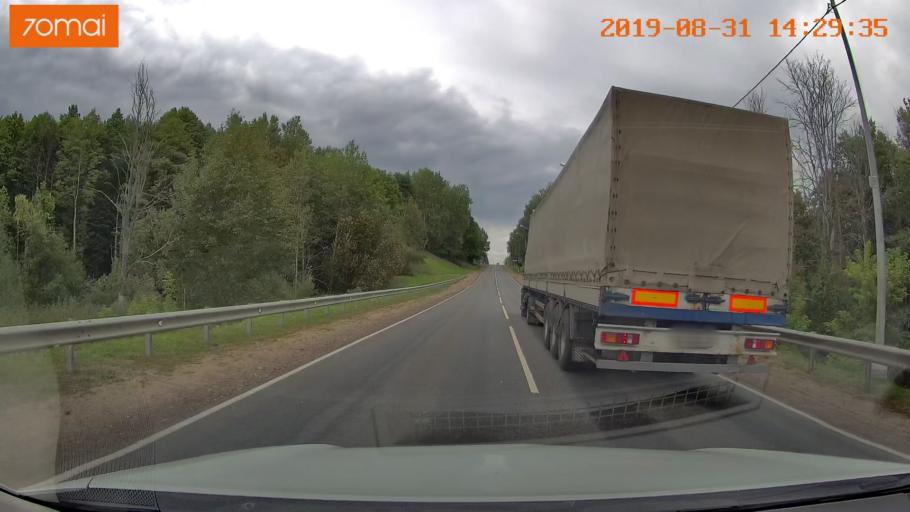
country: RU
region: Smolensk
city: Yekimovichi
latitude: 54.1267
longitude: 33.3346
